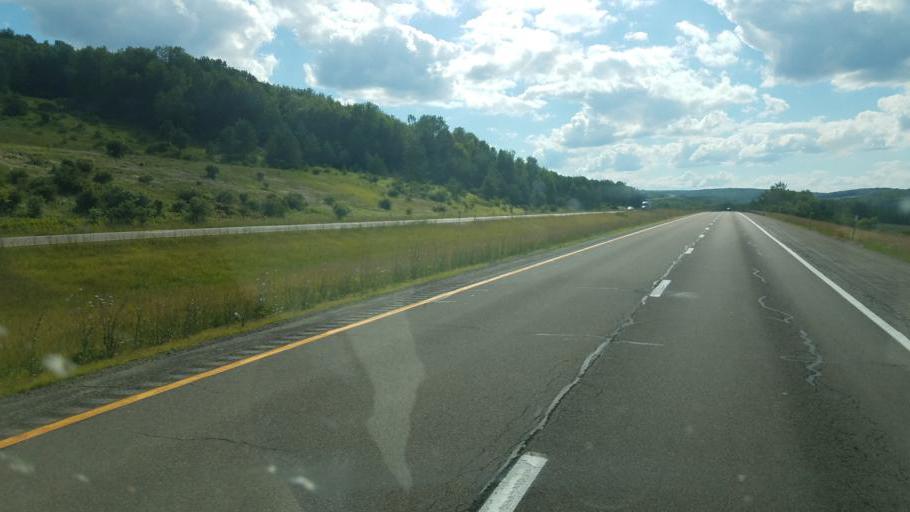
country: US
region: New York
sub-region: Allegany County
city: Alfred
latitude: 42.3173
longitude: -77.7935
